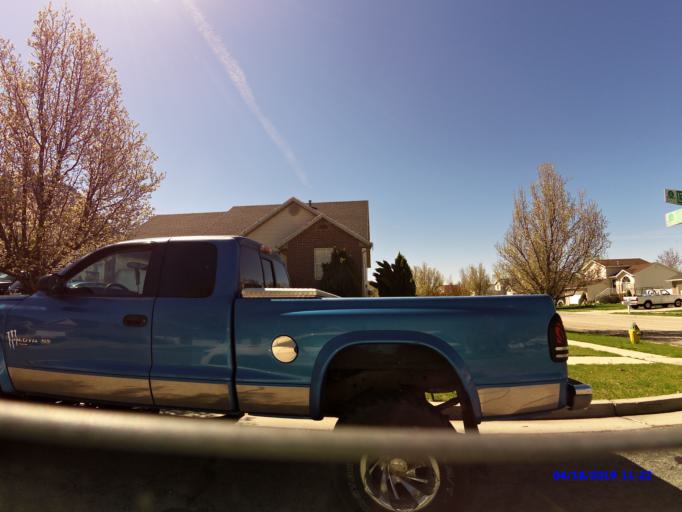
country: US
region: Utah
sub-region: Weber County
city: North Ogden
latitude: 41.2825
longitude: -111.9567
